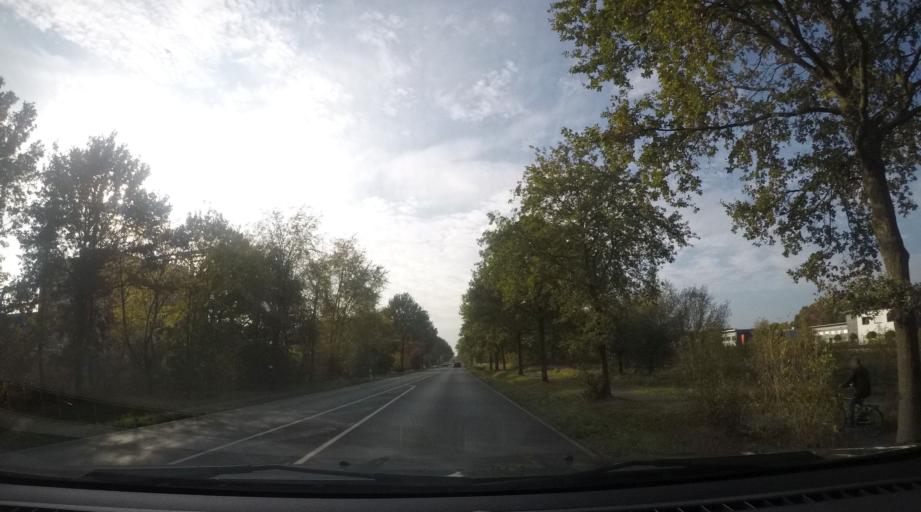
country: DE
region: North Rhine-Westphalia
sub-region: Regierungsbezirk Munster
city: Rhede
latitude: 51.8383
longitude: 6.6578
